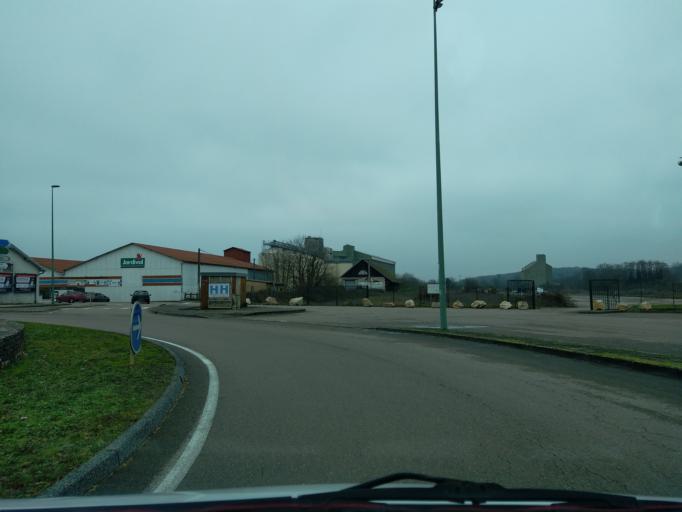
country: FR
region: Franche-Comte
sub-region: Departement de la Haute-Saone
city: Arc-les-Gray
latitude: 47.4514
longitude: 5.5785
